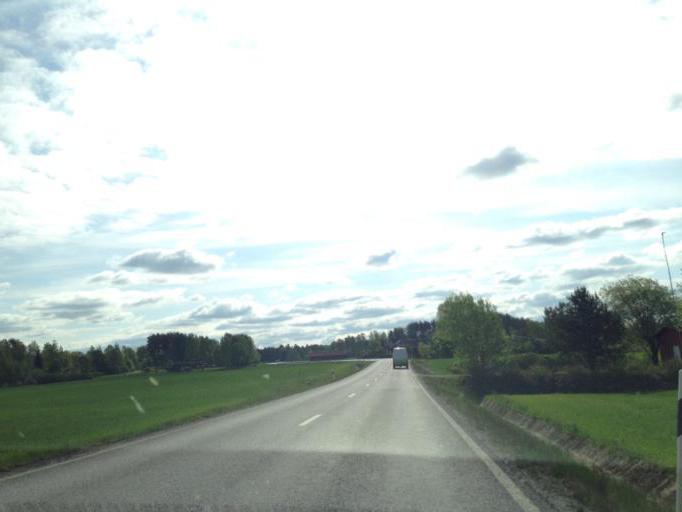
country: SE
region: Soedermanland
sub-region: Nykopings Kommun
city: Stigtomta
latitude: 58.8762
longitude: 16.8700
